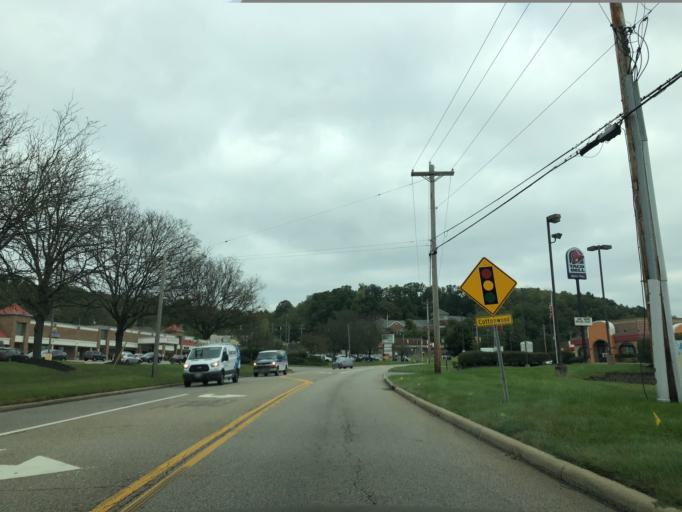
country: US
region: Ohio
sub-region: Hamilton County
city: The Village of Indian Hill
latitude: 39.2531
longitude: -84.2961
